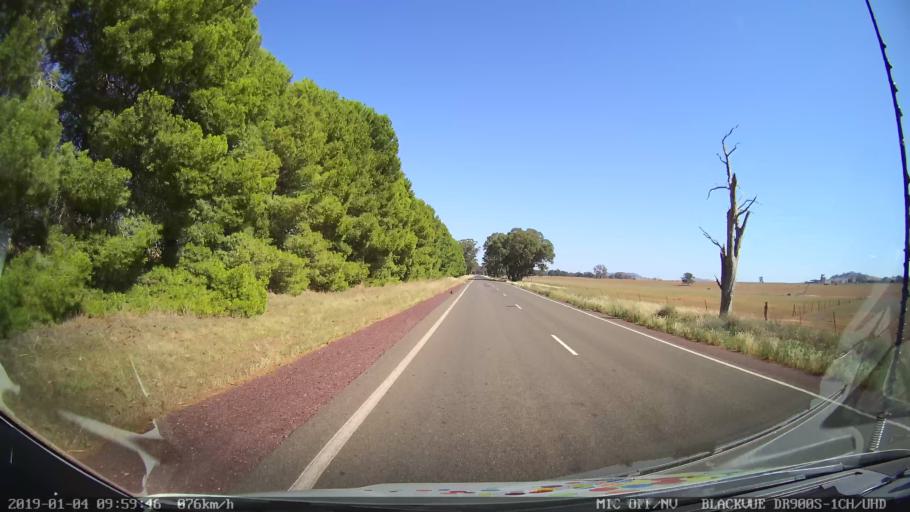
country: AU
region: New South Wales
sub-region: Cabonne
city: Canowindra
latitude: -33.5043
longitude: 148.3838
